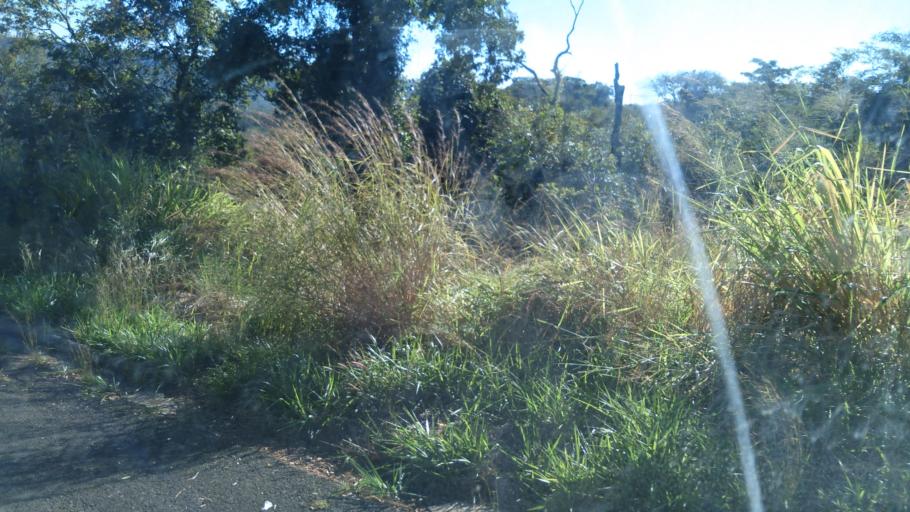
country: BR
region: Goias
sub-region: Mineiros
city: Mineiros
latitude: -17.5453
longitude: -52.5610
